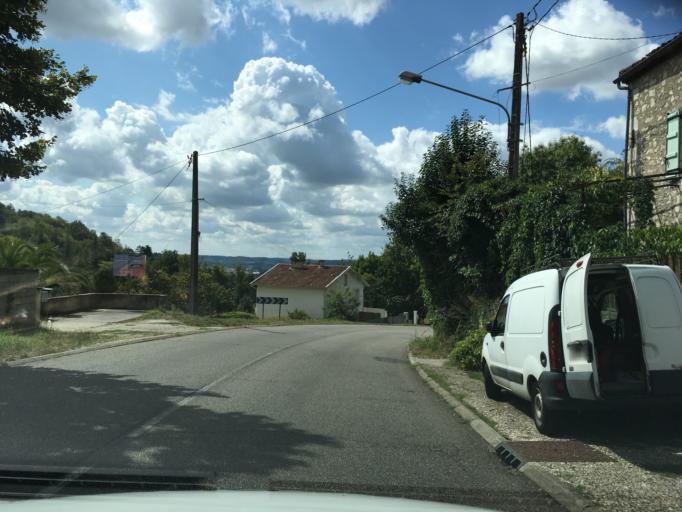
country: FR
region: Aquitaine
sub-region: Departement du Lot-et-Garonne
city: Agen
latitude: 44.2205
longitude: 0.6308
